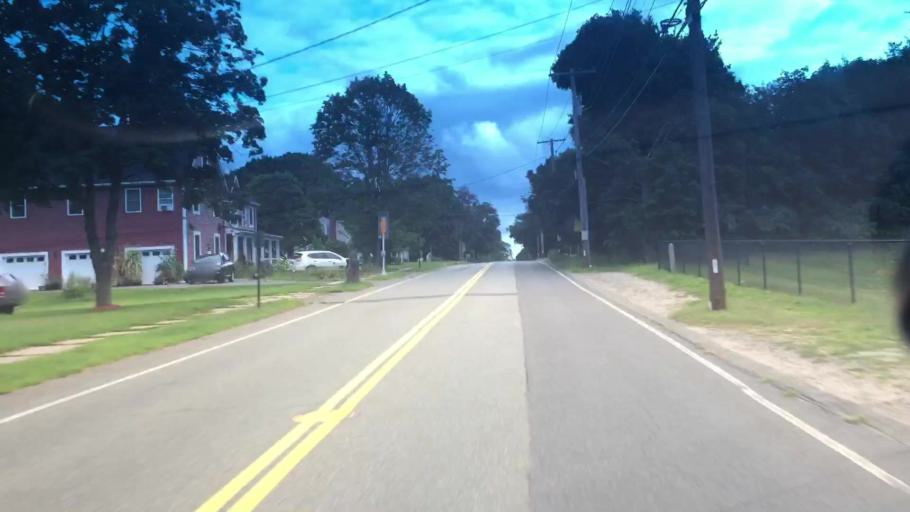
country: US
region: Massachusetts
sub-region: Norfolk County
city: Walpole
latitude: 42.1508
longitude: -71.2306
